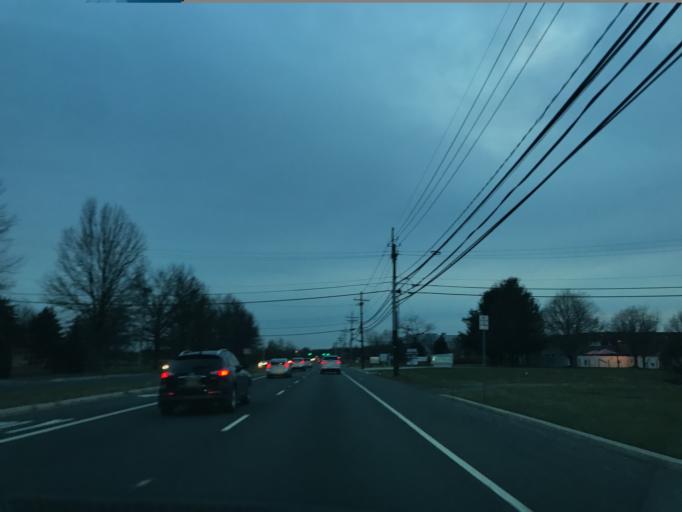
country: US
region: New Jersey
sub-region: Middlesex County
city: Rossmoor
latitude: 40.3419
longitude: -74.5004
